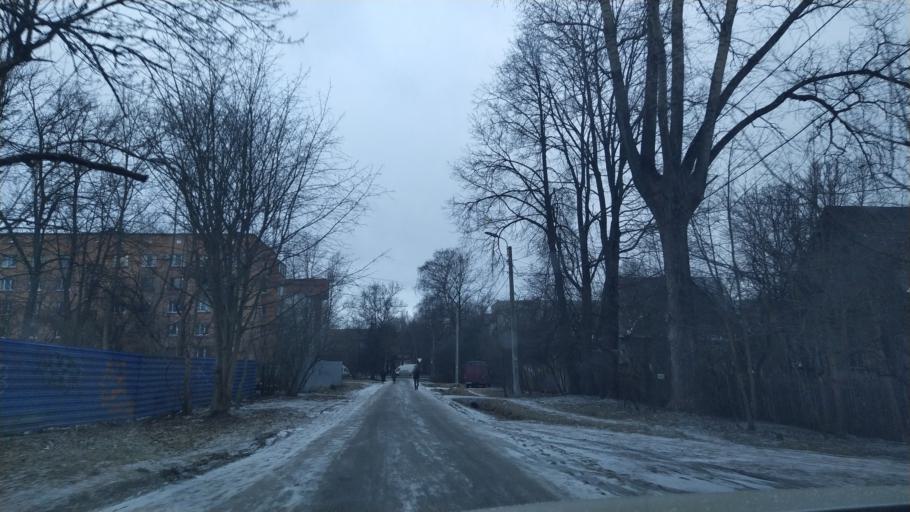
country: RU
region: St.-Petersburg
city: Pushkin
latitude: 59.7276
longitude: 30.4102
